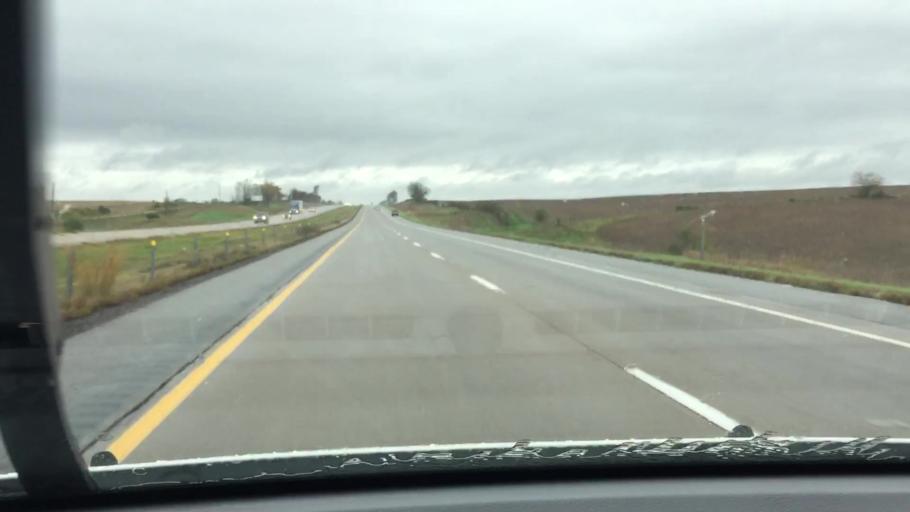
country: US
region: Iowa
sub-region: Poweshiek County
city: Brooklyn
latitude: 41.6963
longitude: -92.4046
